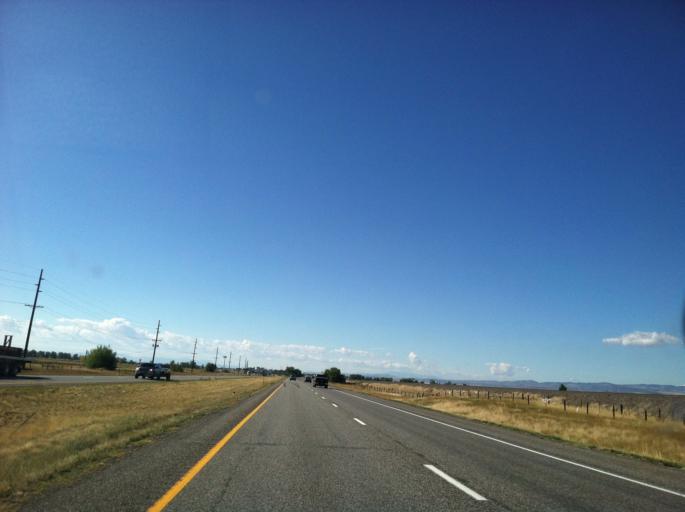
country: US
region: Montana
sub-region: Gallatin County
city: Belgrade
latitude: 45.7422
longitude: -111.1141
